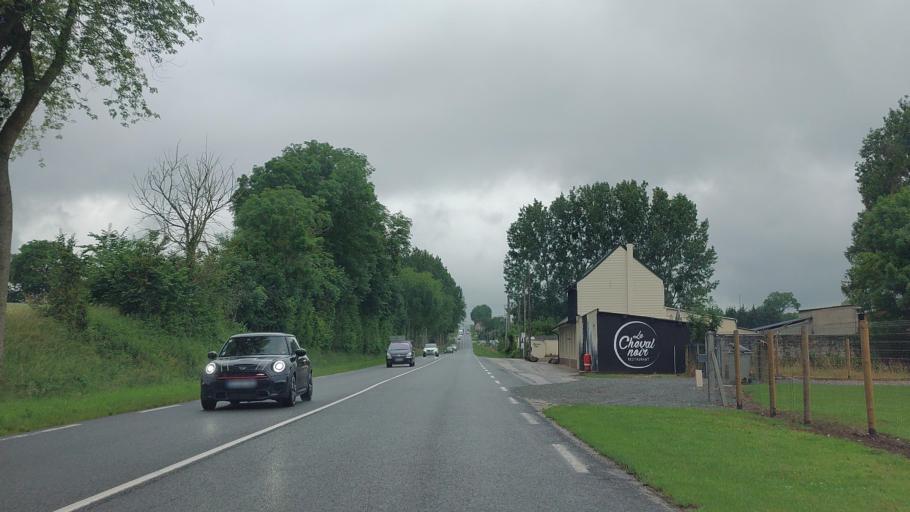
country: FR
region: Picardie
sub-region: Departement de la Somme
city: Chepy
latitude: 50.0877
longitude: 1.6746
